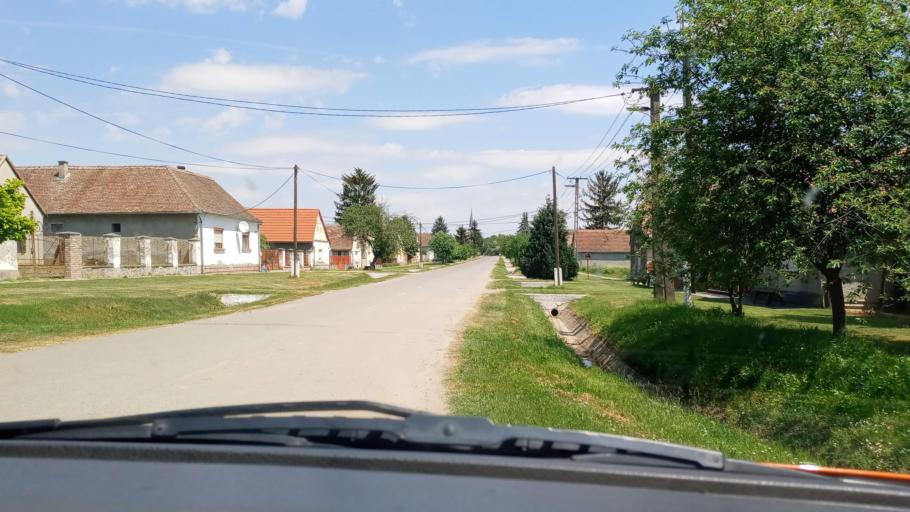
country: HR
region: Osjecko-Baranjska
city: Viljevo
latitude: 45.8270
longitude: 18.1317
